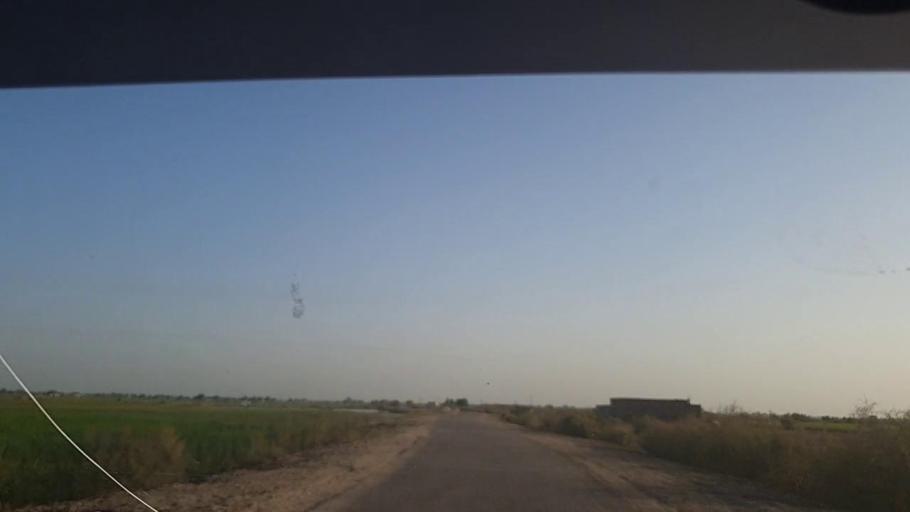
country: PK
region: Sindh
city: Thul
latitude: 28.1430
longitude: 68.8876
